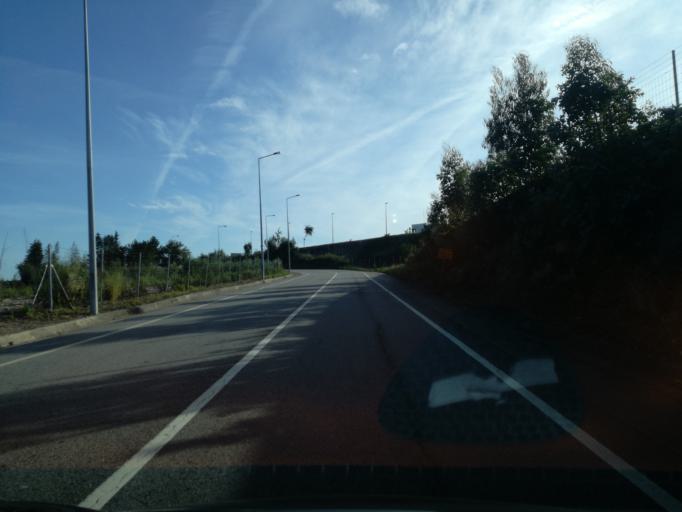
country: PT
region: Porto
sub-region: Trofa
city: Sao Romao do Coronado
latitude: 41.2850
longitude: -8.5167
